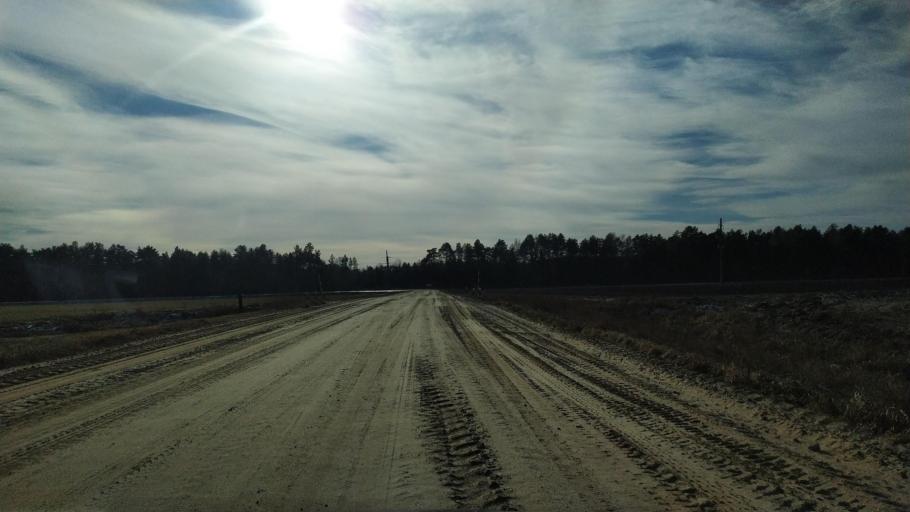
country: BY
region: Brest
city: Pruzhany
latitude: 52.5604
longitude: 24.2924
